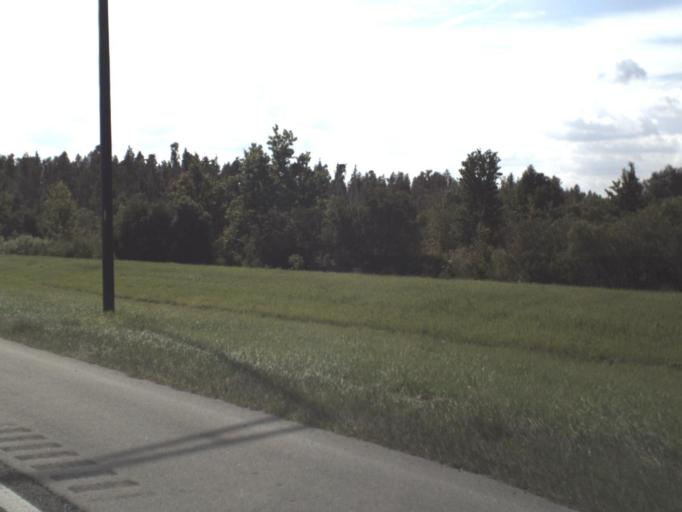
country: US
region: Florida
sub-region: Polk County
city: Winston
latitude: 28.0177
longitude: -82.0366
